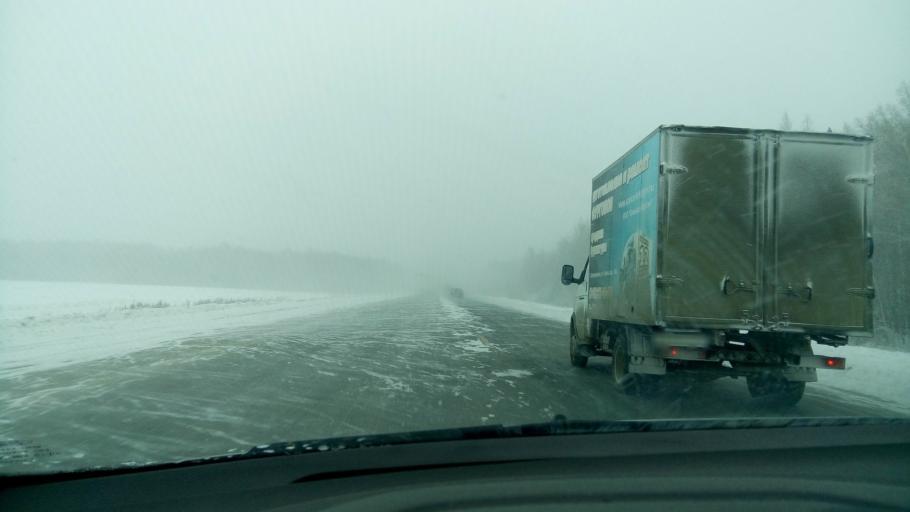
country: RU
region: Sverdlovsk
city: Bogdanovich
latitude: 56.7743
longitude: 61.9522
